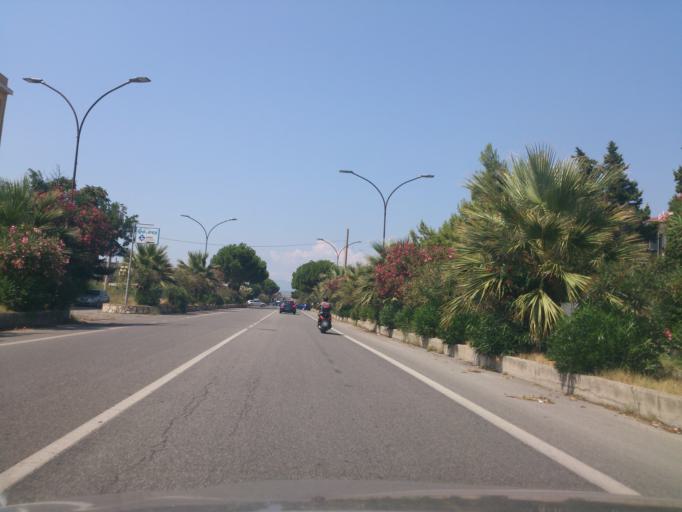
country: IT
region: Calabria
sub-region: Provincia di Reggio Calabria
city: Marina di Gioiosa Ionica
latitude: 38.3045
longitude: 16.3374
